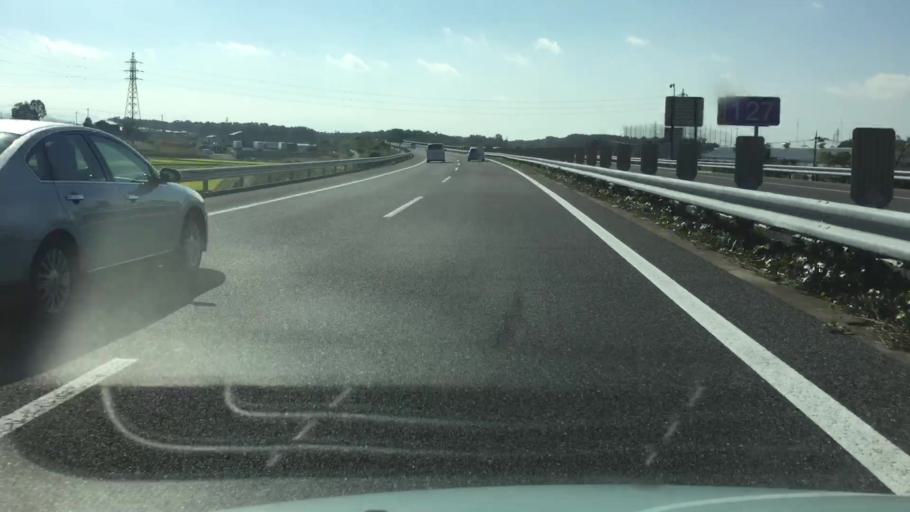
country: JP
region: Tochigi
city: Mooka
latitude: 36.4365
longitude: 139.9704
